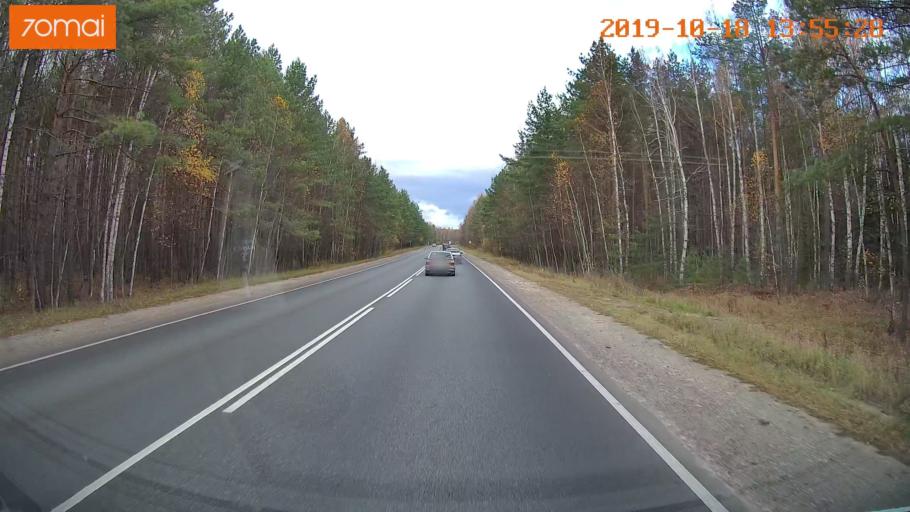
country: RU
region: Rjazan
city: Spas-Klepiki
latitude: 55.0526
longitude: 40.0236
